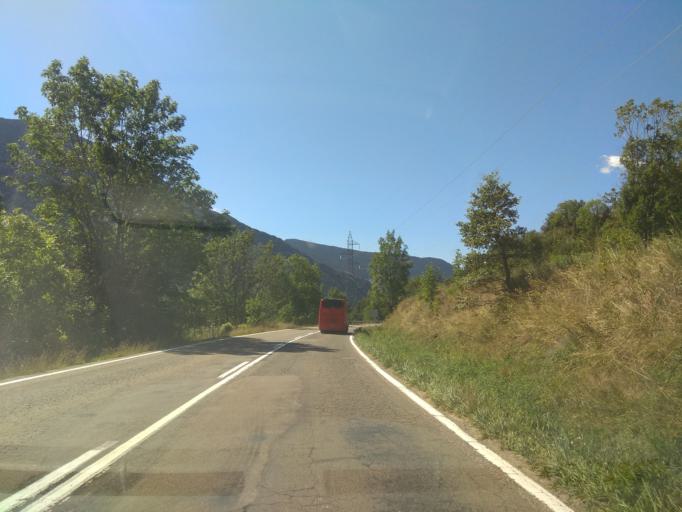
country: ES
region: Catalonia
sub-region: Provincia de Lleida
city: Vielha
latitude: 42.5288
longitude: 0.8311
